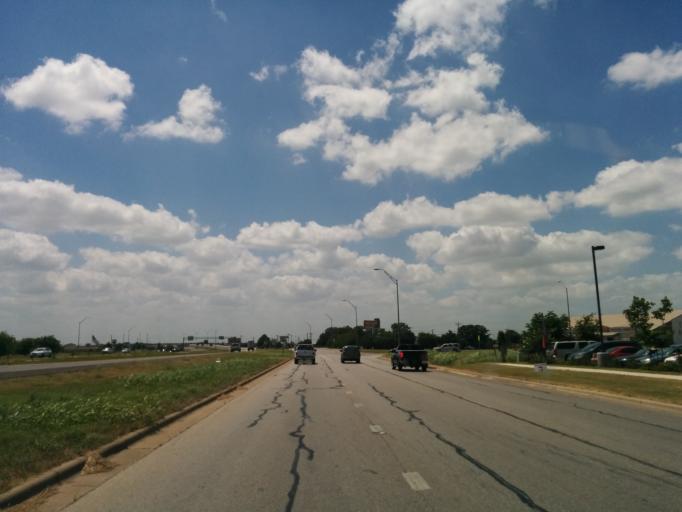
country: US
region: Texas
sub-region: Bastrop County
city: Bastrop
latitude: 30.1100
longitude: -97.3419
